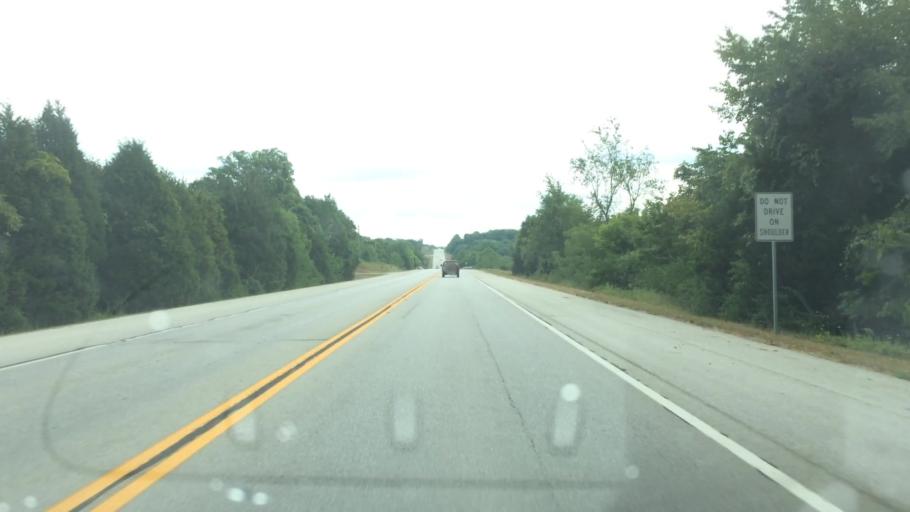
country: US
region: Missouri
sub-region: Greene County
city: Springfield
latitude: 37.1796
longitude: -93.2042
